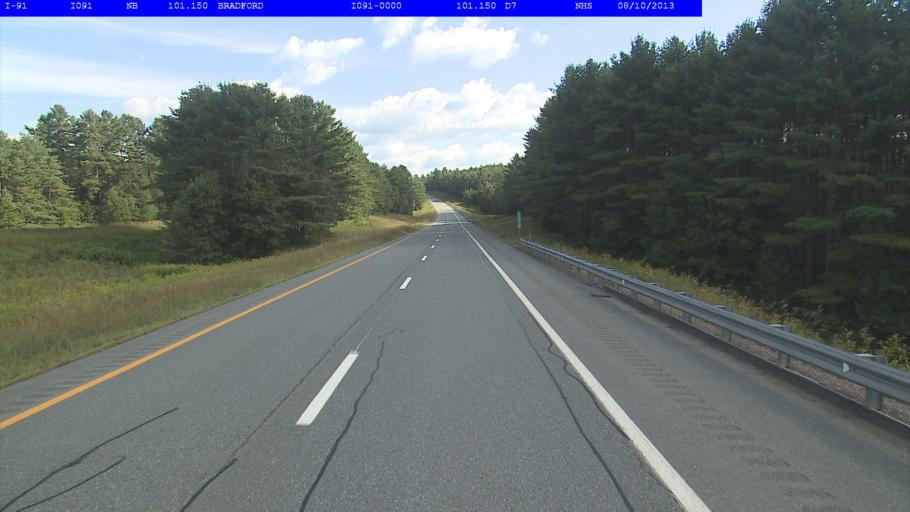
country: US
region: New Hampshire
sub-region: Grafton County
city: Haverhill
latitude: 44.0306
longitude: -72.1126
